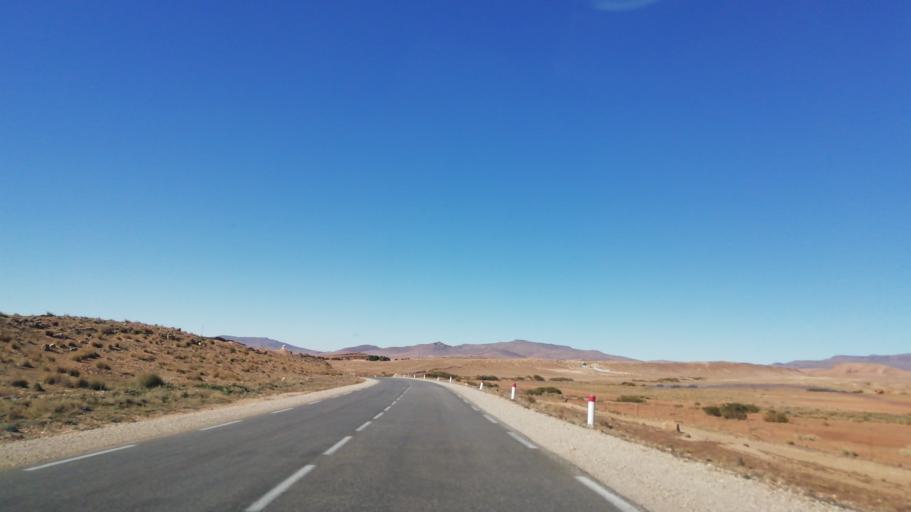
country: DZ
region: El Bayadh
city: El Bayadh
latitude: 33.6086
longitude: 1.2420
